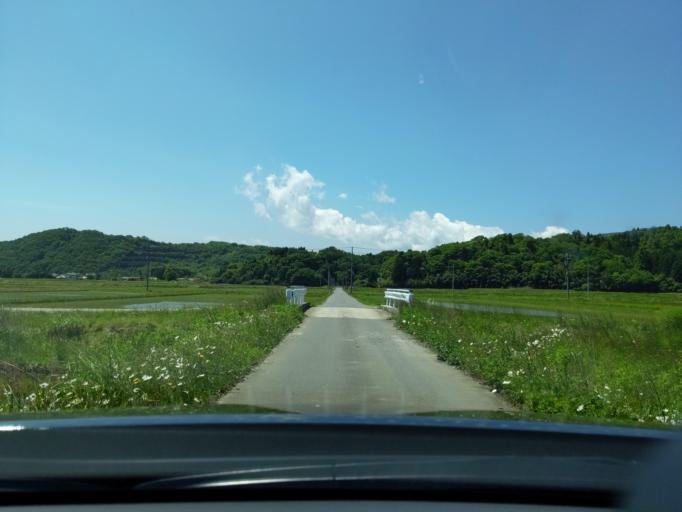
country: JP
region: Fukushima
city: Koriyama
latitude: 37.4042
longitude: 140.2574
